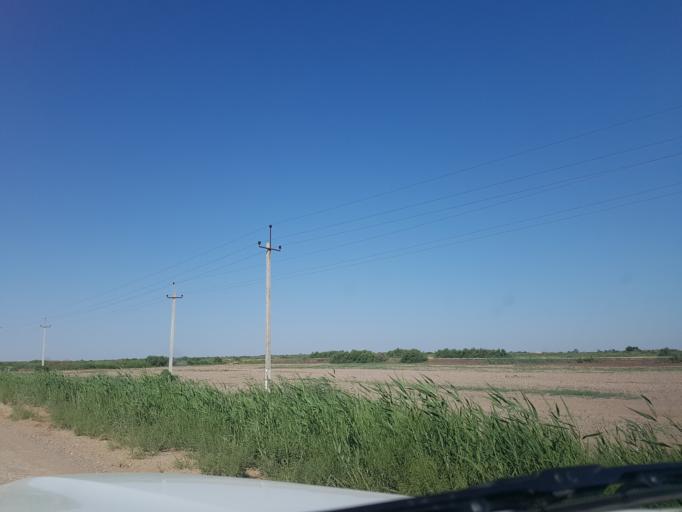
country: TM
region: Dasoguz
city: Koeneuergench
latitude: 42.1312
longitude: 58.9469
